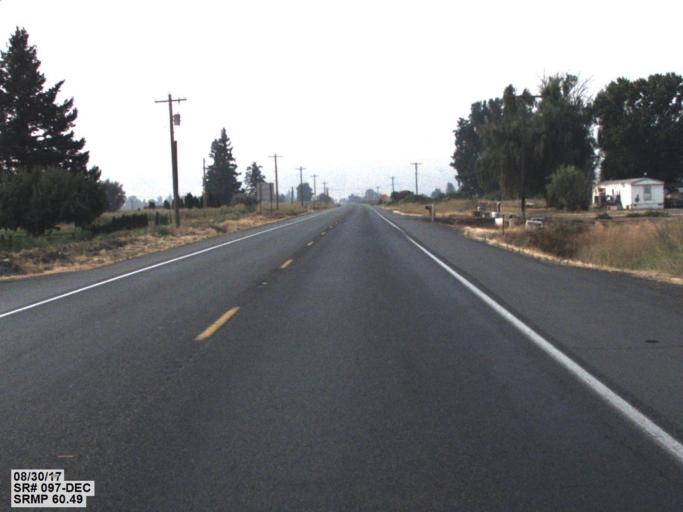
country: US
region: Washington
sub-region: Yakima County
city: Toppenish
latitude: 46.3566
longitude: -120.3203
